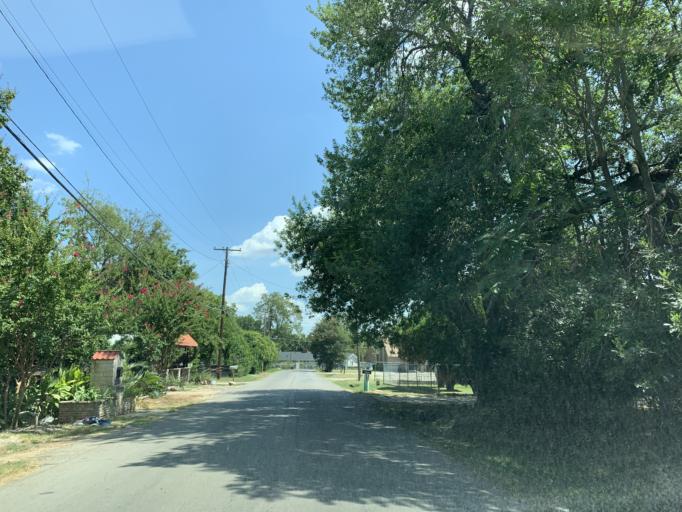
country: US
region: Texas
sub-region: Dallas County
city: Hutchins
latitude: 32.7123
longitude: -96.7652
